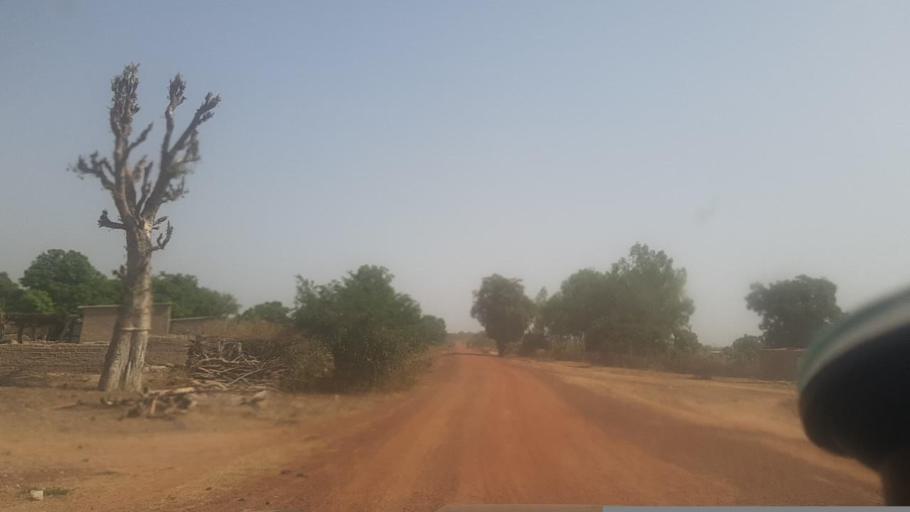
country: ML
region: Segou
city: Segou
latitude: 12.9321
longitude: -6.2867
